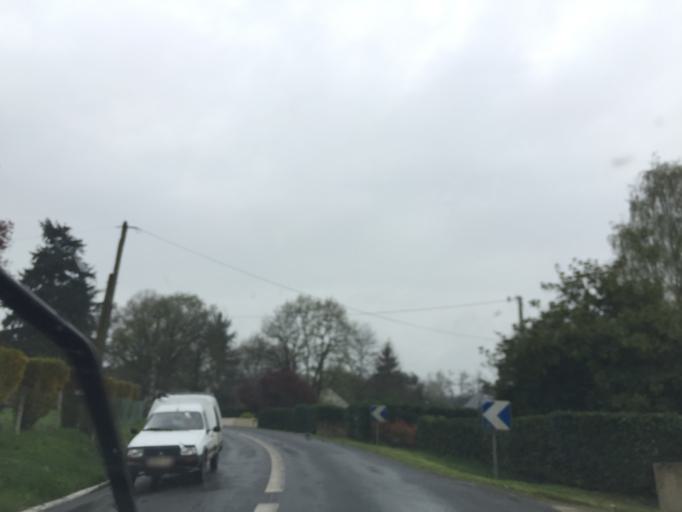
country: FR
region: Pays de la Loire
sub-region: Departement de la Loire-Atlantique
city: Casson
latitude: 47.4124
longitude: -1.5335
